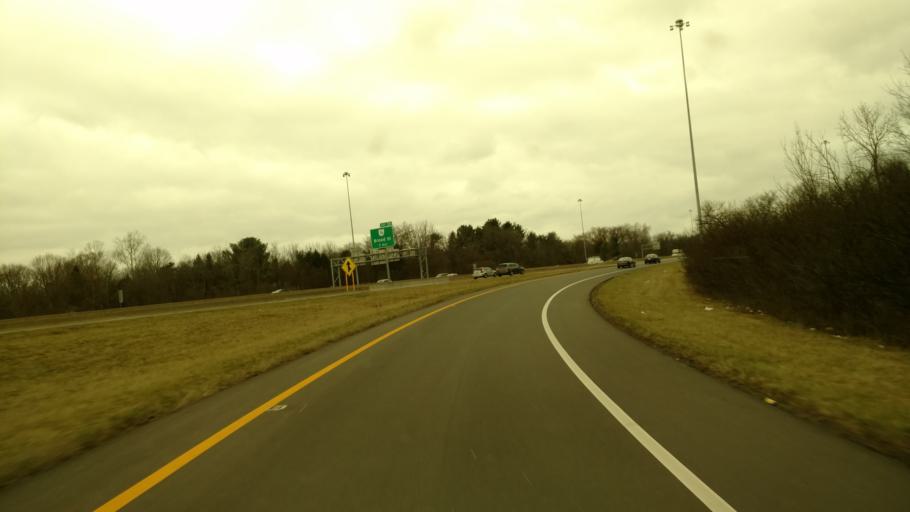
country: US
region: Ohio
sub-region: Franklin County
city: Reynoldsburg
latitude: 39.9572
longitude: -82.8429
